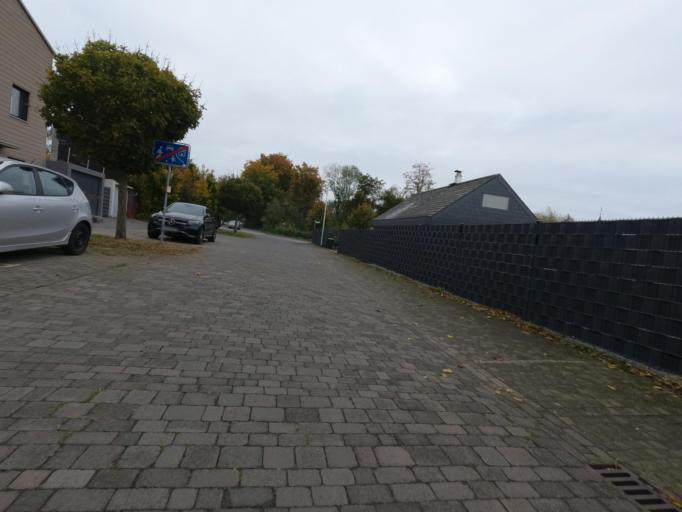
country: DE
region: North Rhine-Westphalia
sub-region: Regierungsbezirk Koln
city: Linnich
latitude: 50.9660
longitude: 6.3168
